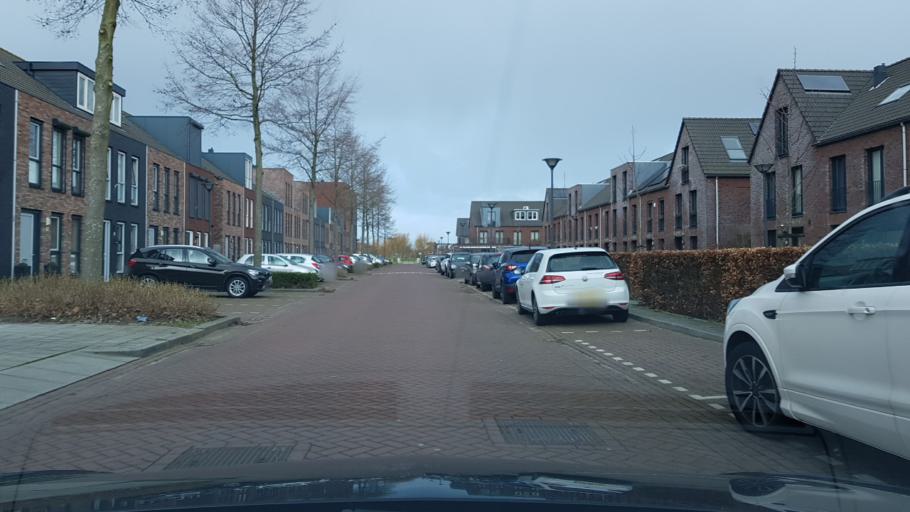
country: NL
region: North Holland
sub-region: Gemeente Bloemendaal
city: Bennebroek
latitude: 52.3031
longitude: 4.6345
